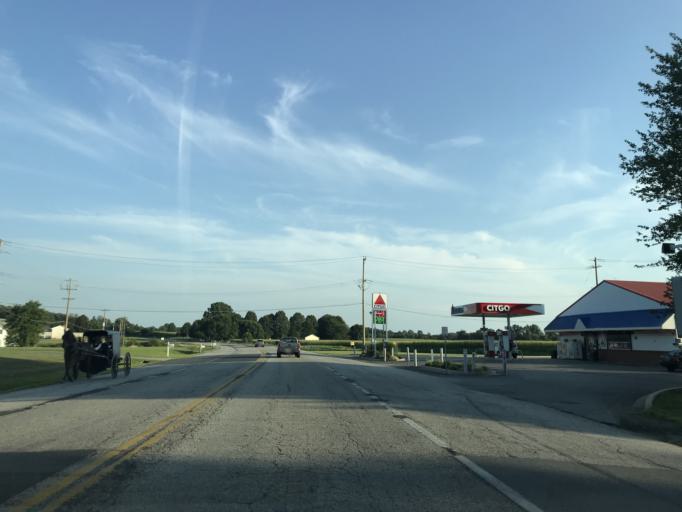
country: US
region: Maryland
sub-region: Cecil County
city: Rising Sun
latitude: 39.6976
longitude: -75.9790
